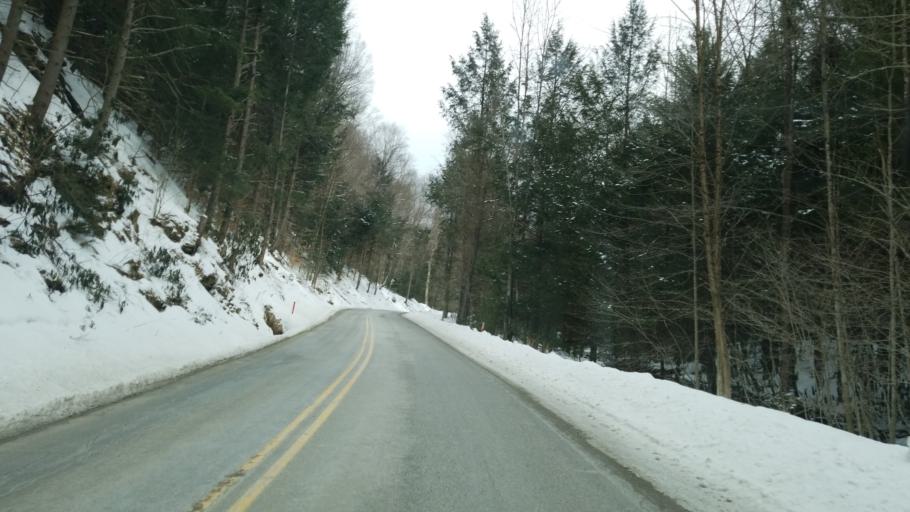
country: US
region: Pennsylvania
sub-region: Clearfield County
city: Shiloh
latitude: 41.2535
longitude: -78.1519
